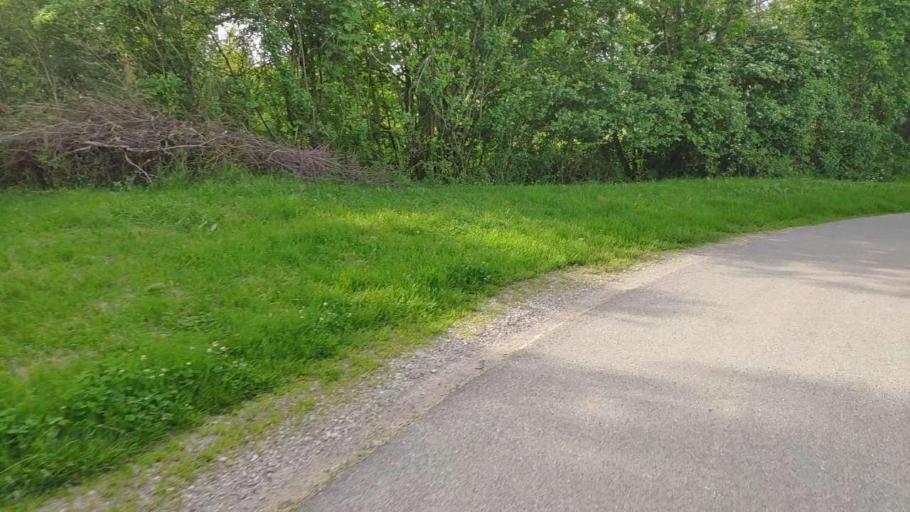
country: FR
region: Franche-Comte
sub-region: Departement du Jura
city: Bletterans
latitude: 46.7387
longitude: 5.4693
